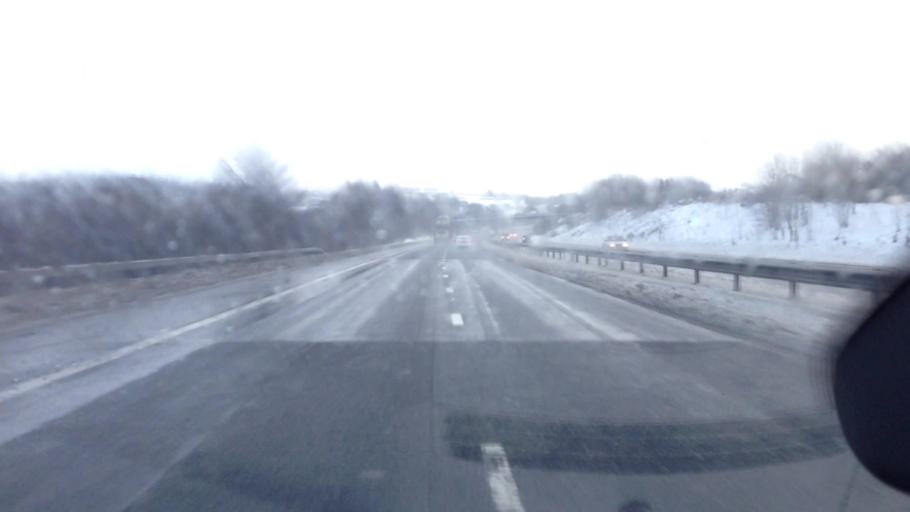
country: GB
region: Scotland
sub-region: South Lanarkshire
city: Lesmahagow
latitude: 55.6528
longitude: -3.8955
